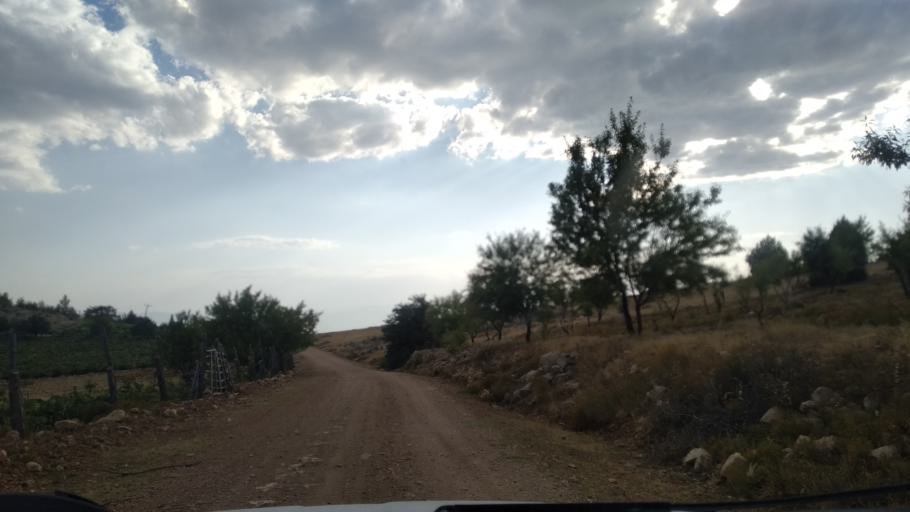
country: TR
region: Mersin
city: Sarikavak
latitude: 36.5932
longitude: 33.6812
